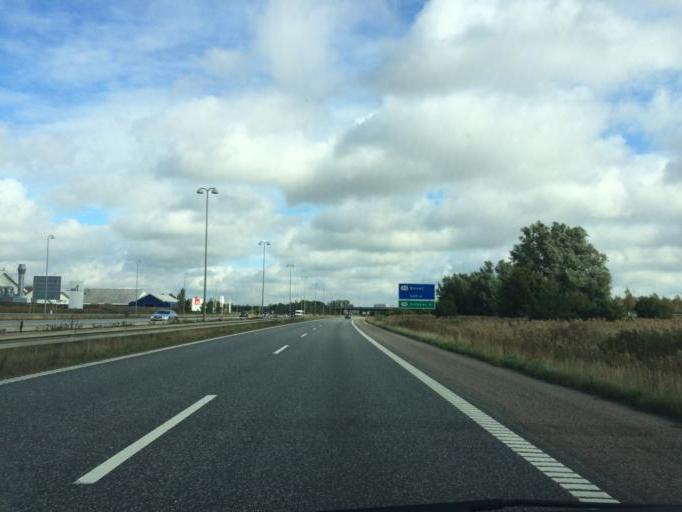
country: DK
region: North Denmark
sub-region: Alborg Kommune
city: Vestbjerg
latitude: 57.0805
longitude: 9.9625
